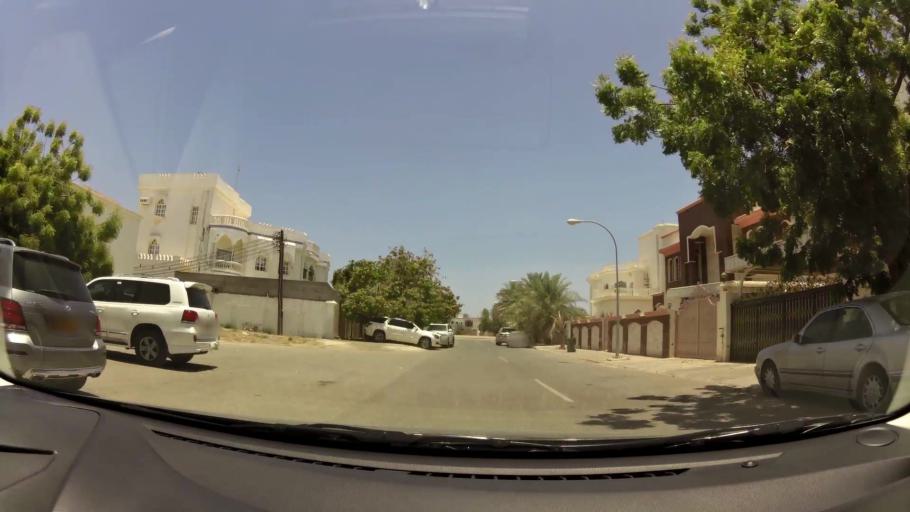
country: OM
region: Muhafazat Masqat
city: Bawshar
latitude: 23.5977
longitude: 58.4063
